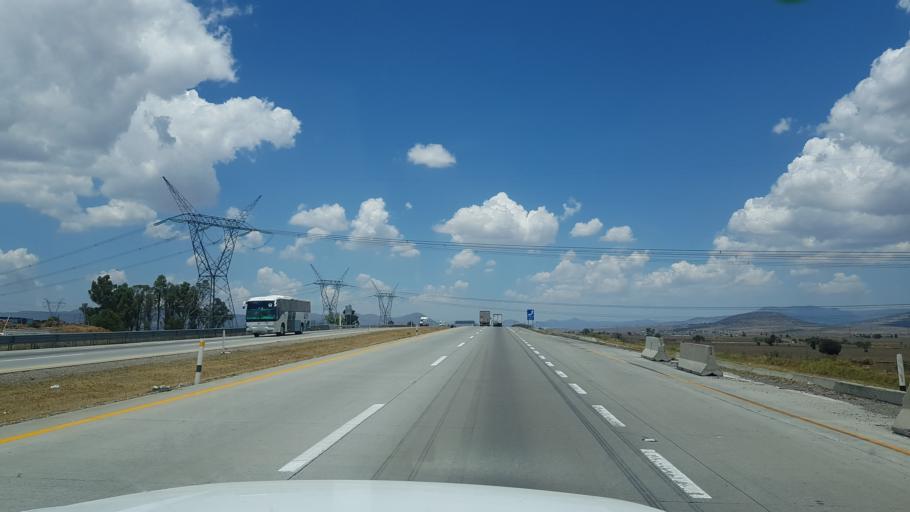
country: MX
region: Tlaxcala
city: Sanctorum
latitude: 19.5554
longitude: -98.4963
